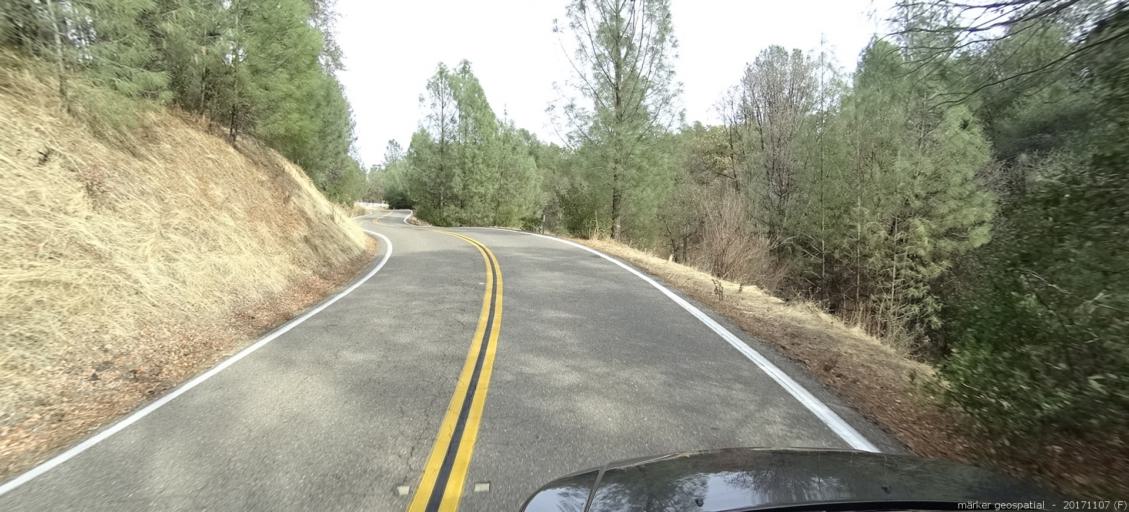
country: US
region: California
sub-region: Shasta County
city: Shasta
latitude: 40.5145
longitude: -122.5179
